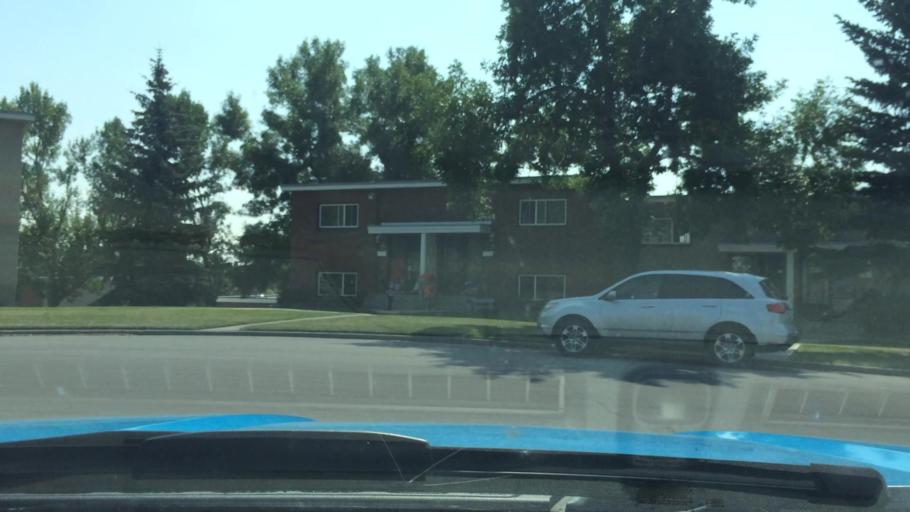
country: CA
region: Alberta
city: Calgary
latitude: 51.0840
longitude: -114.0932
